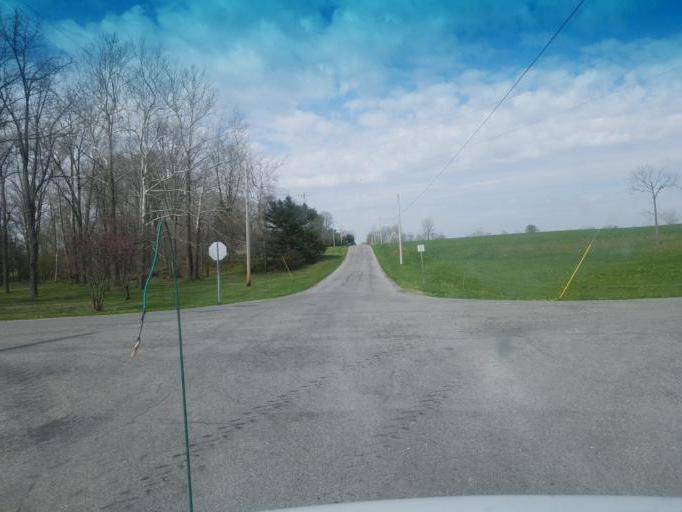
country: US
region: Ohio
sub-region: Logan County
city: Northwood
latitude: 40.4913
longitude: -83.7293
